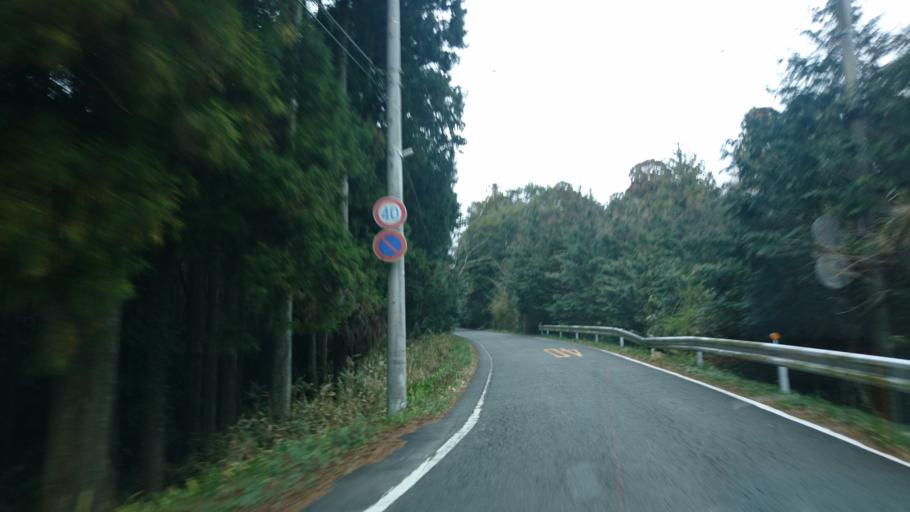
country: JP
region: Shizuoka
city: Fujinomiya
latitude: 35.3229
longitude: 138.5743
